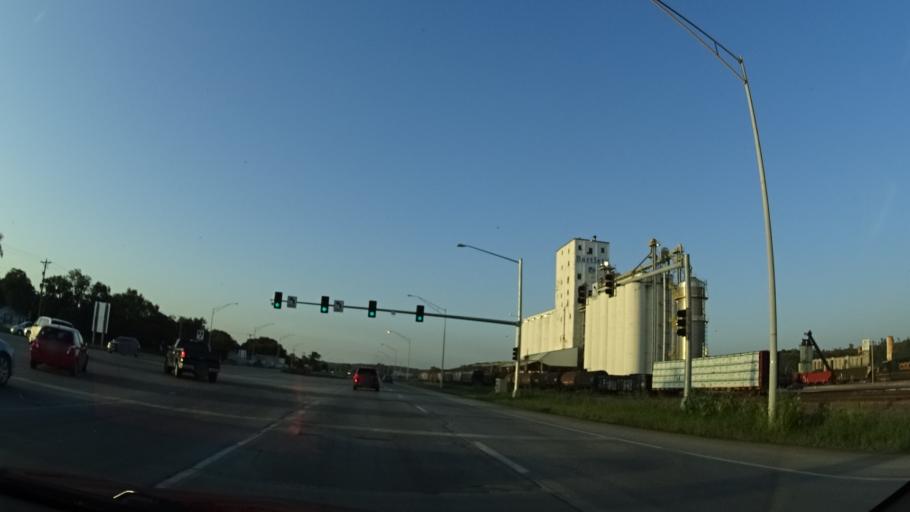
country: US
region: Iowa
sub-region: Pottawattamie County
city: Council Bluffs
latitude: 41.2340
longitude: -95.8513
